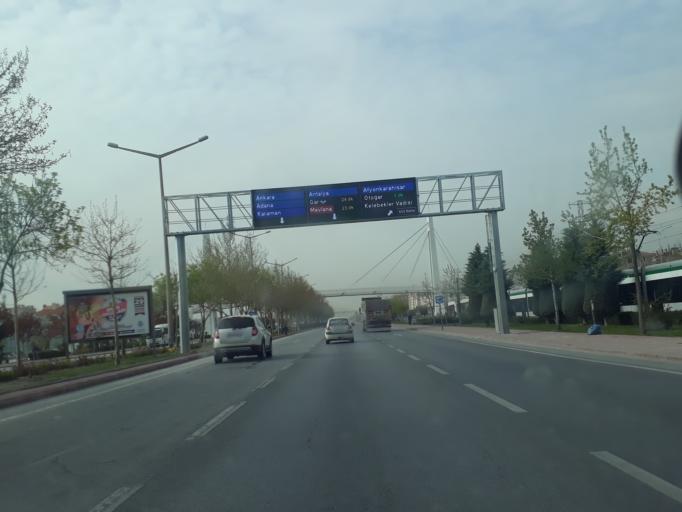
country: TR
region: Konya
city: Selcuklu
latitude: 37.9668
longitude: 32.5151
